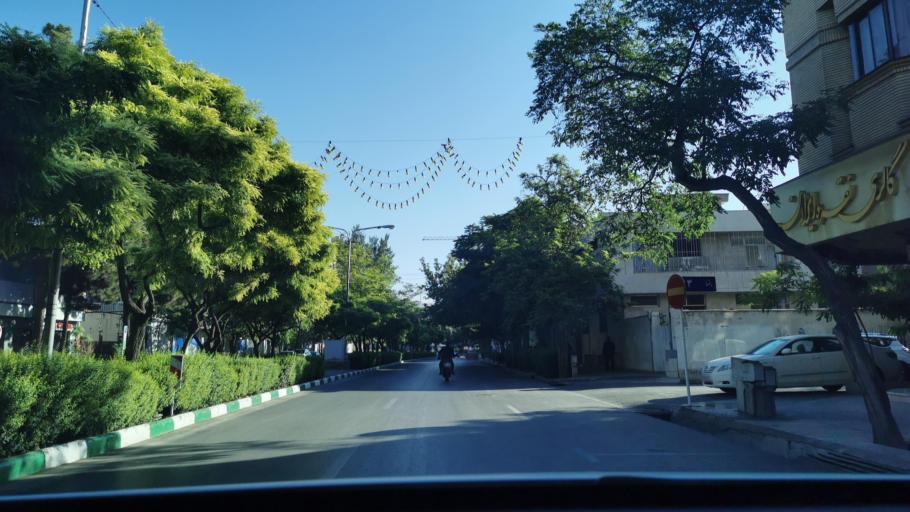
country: IR
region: Razavi Khorasan
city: Mashhad
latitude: 36.2966
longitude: 59.5690
